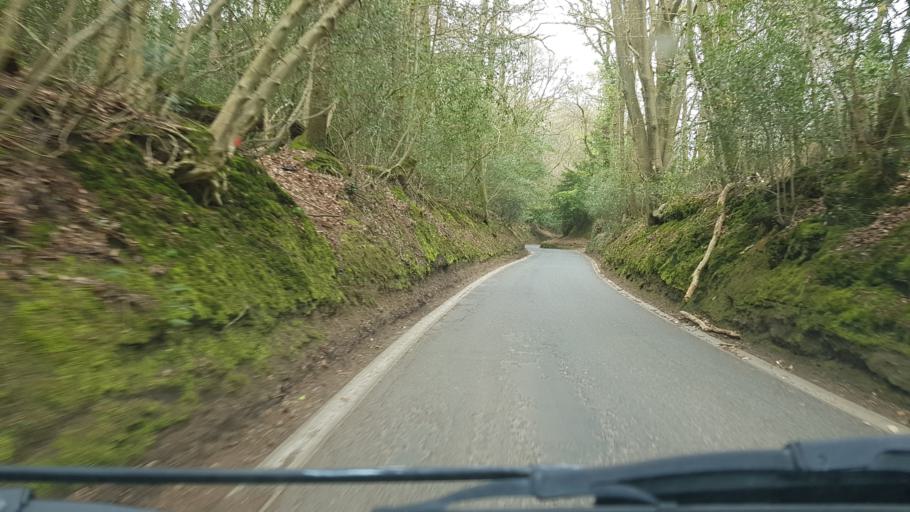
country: GB
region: England
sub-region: Surrey
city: Cranleigh
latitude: 51.1842
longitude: -0.4628
